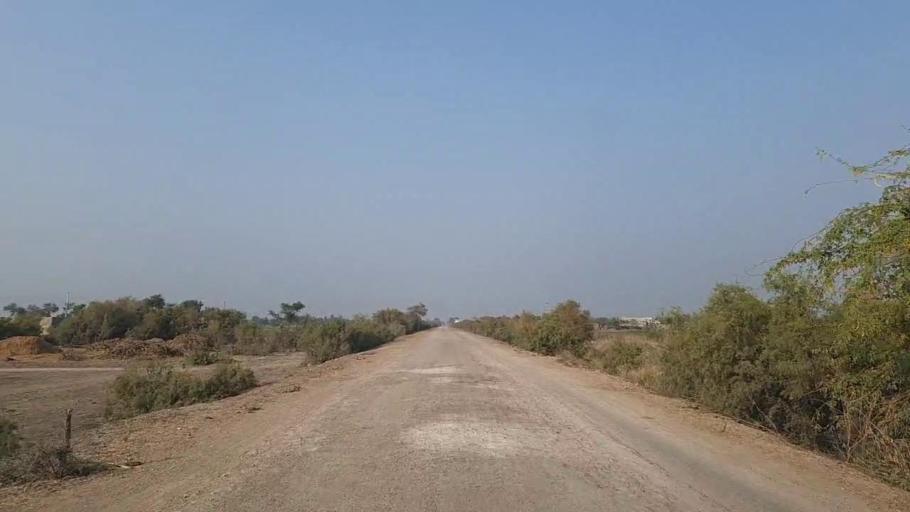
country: PK
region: Sindh
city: Nawabshah
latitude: 26.3349
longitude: 68.4891
